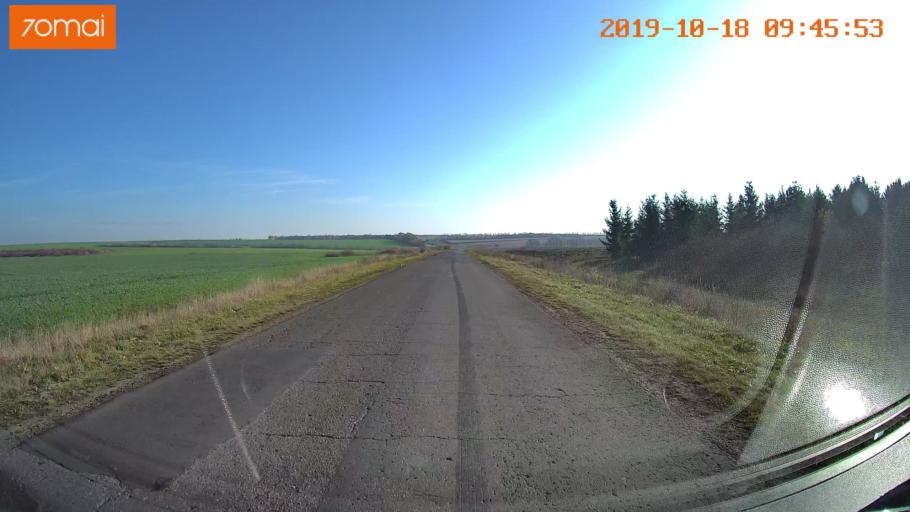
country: RU
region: Tula
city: Kazachka
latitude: 53.3123
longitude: 38.1994
